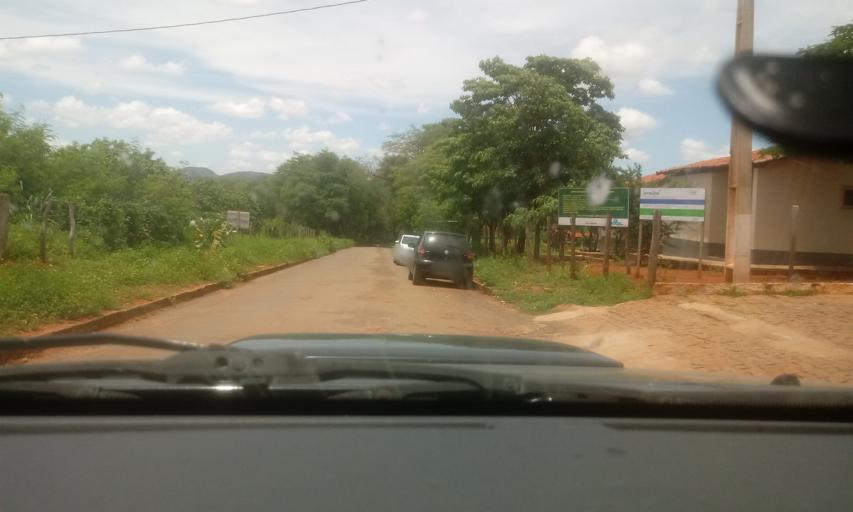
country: BR
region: Bahia
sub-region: Riacho De Santana
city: Riacho de Santana
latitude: -13.6015
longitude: -42.9459
